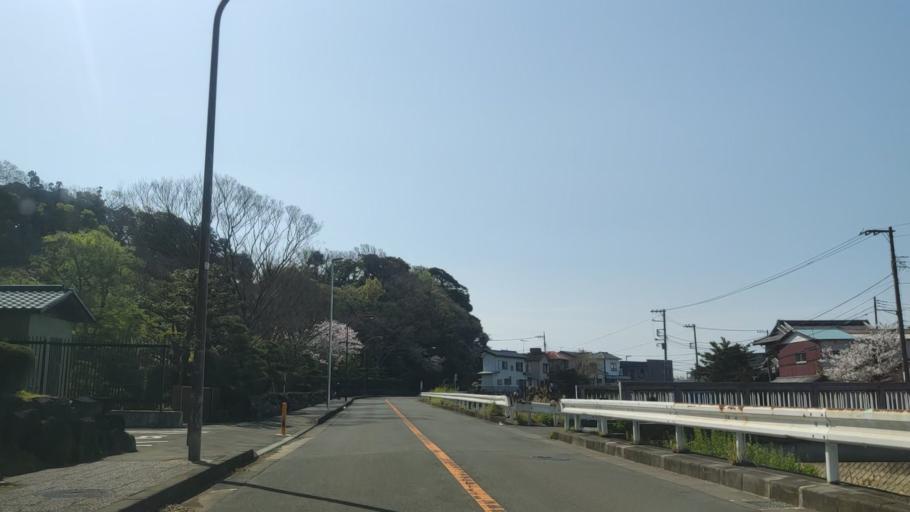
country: JP
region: Kanagawa
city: Oiso
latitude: 35.3068
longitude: 139.2886
